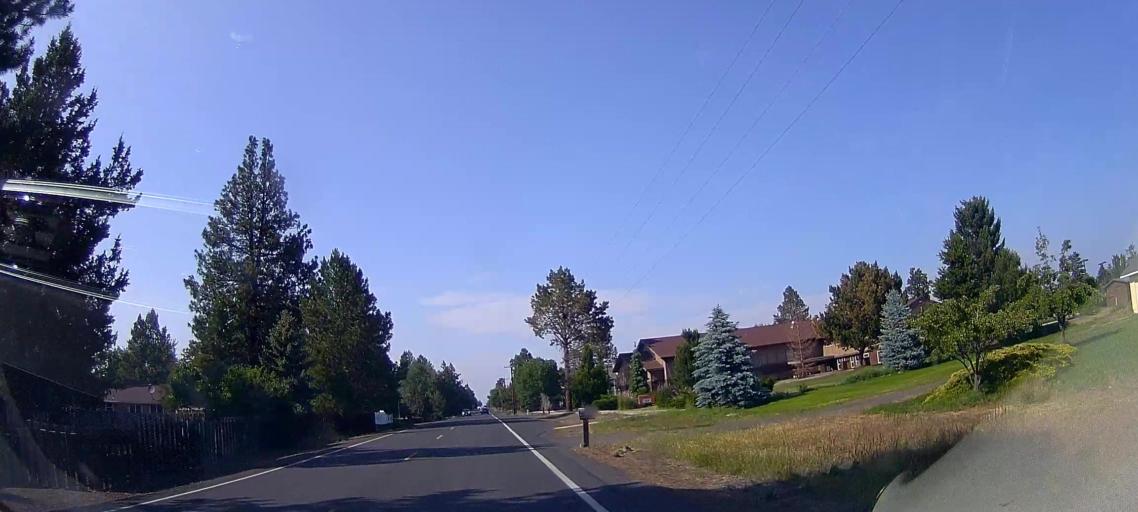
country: US
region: Oregon
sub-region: Deschutes County
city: Bend
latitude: 44.0396
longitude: -121.2687
